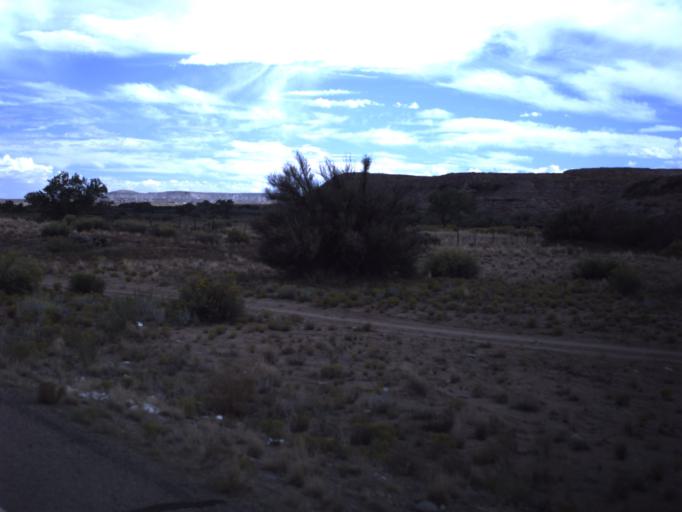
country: US
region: Utah
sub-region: San Juan County
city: Blanding
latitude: 37.2712
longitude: -109.3259
